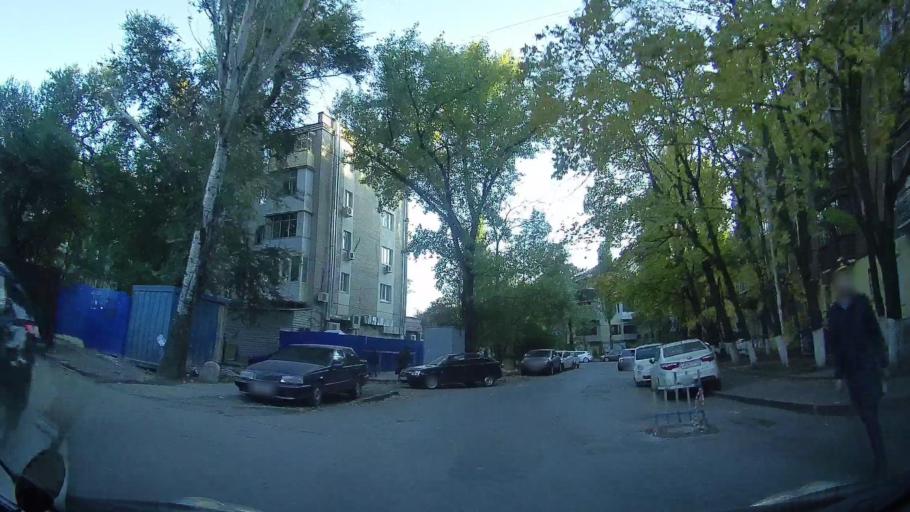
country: RU
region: Rostov
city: Rostov-na-Donu
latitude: 47.2377
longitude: 39.7028
